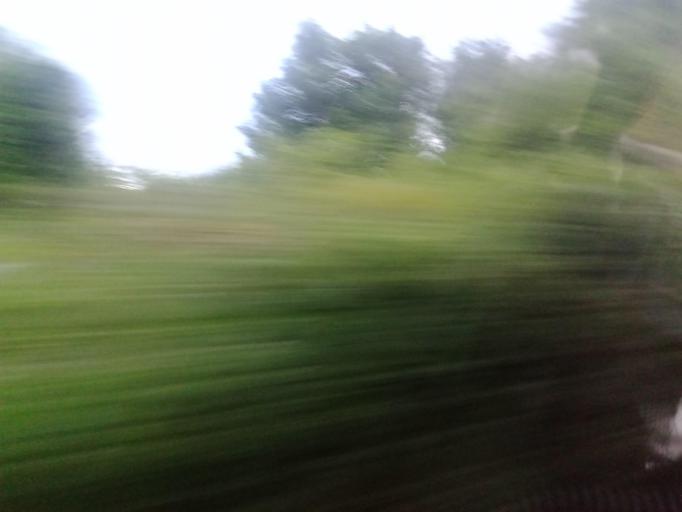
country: IE
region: Leinster
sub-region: Laois
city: Mountmellick
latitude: 53.1118
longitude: -7.3573
